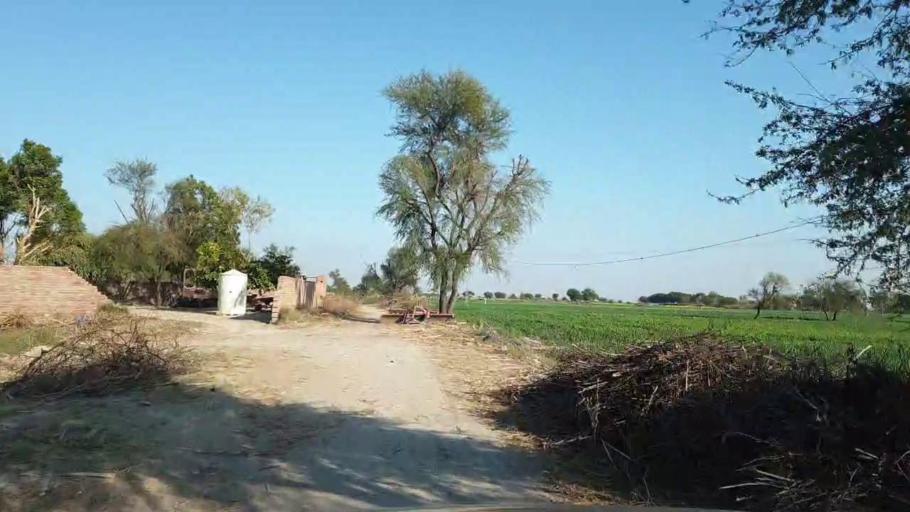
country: PK
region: Sindh
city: Khadro
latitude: 26.2035
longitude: 68.7618
